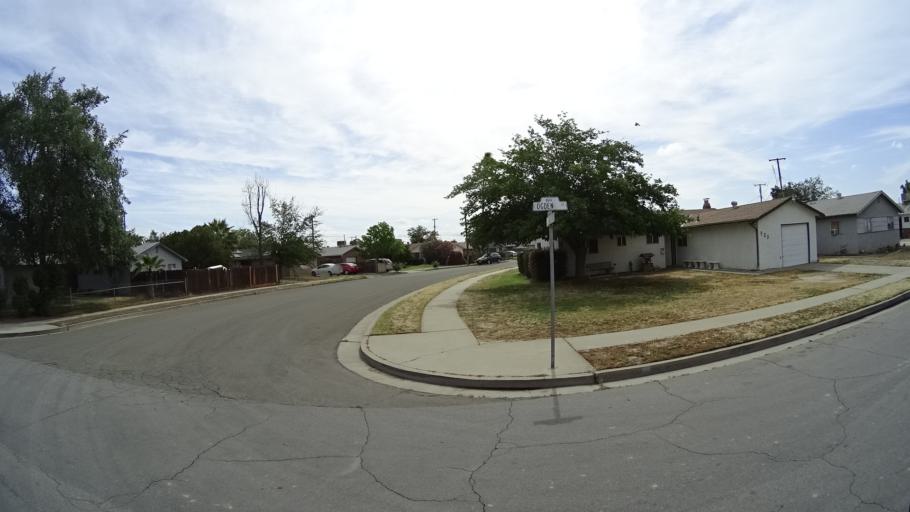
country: US
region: California
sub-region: Kings County
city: Hanford
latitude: 36.3159
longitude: -119.6703
